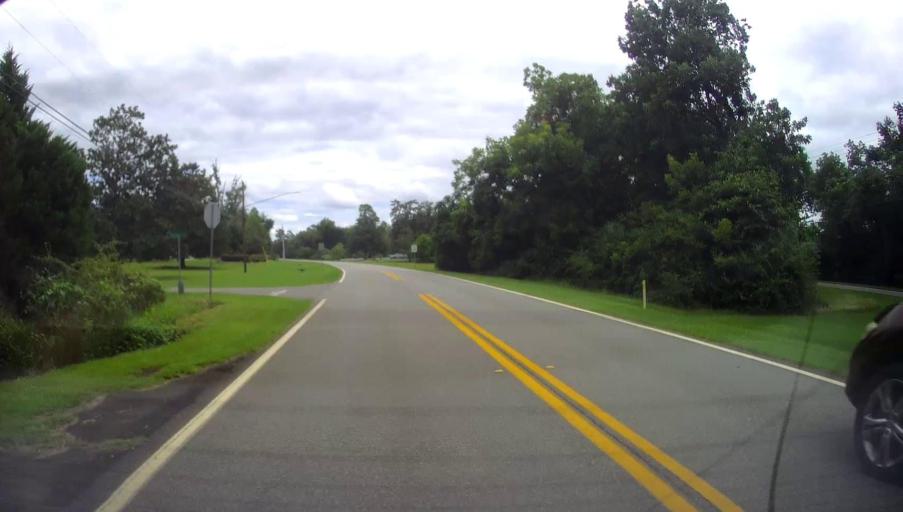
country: US
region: Georgia
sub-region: Twiggs County
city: Jeffersonville
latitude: 32.6813
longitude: -83.3347
